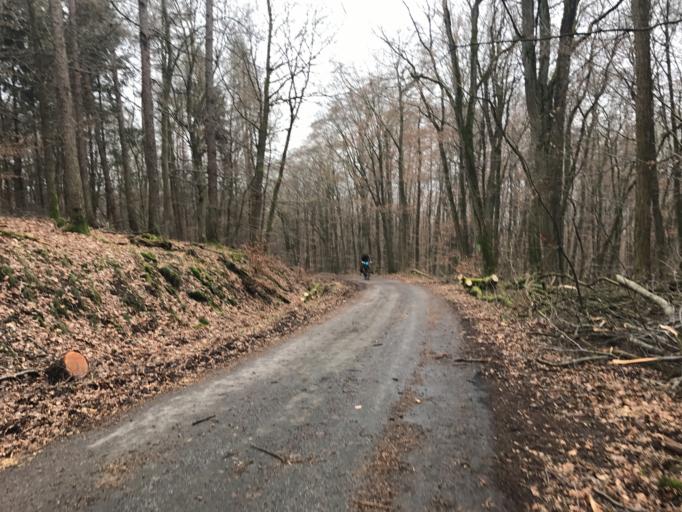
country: DE
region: Hesse
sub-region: Regierungsbezirk Darmstadt
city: Wiesbaden
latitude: 50.1251
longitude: 8.2271
